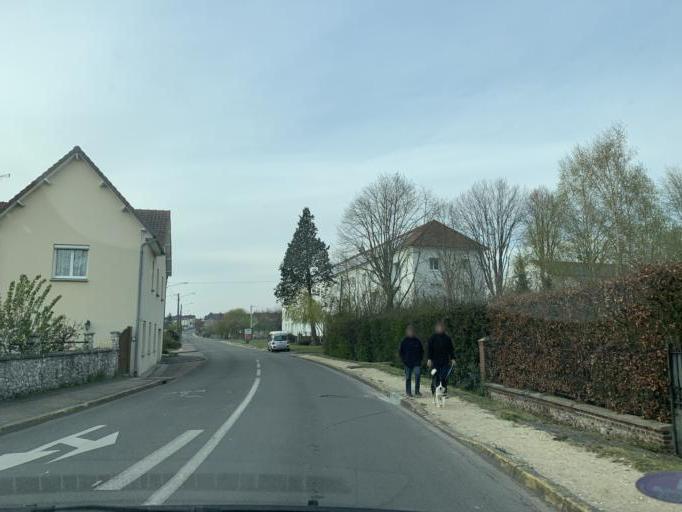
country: FR
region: Haute-Normandie
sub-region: Departement de la Seine-Maritime
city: La Mailleraye-sur-Seine
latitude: 49.4781
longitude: 0.7749
